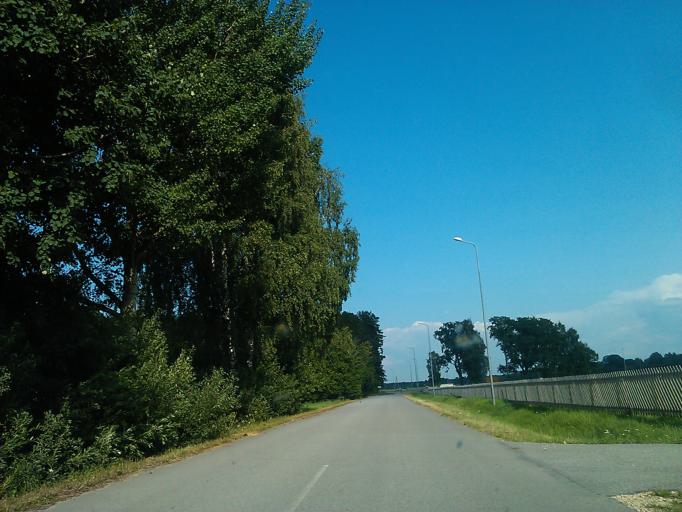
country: LV
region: Saulkrastu
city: Saulkrasti
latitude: 57.4079
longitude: 24.4267
